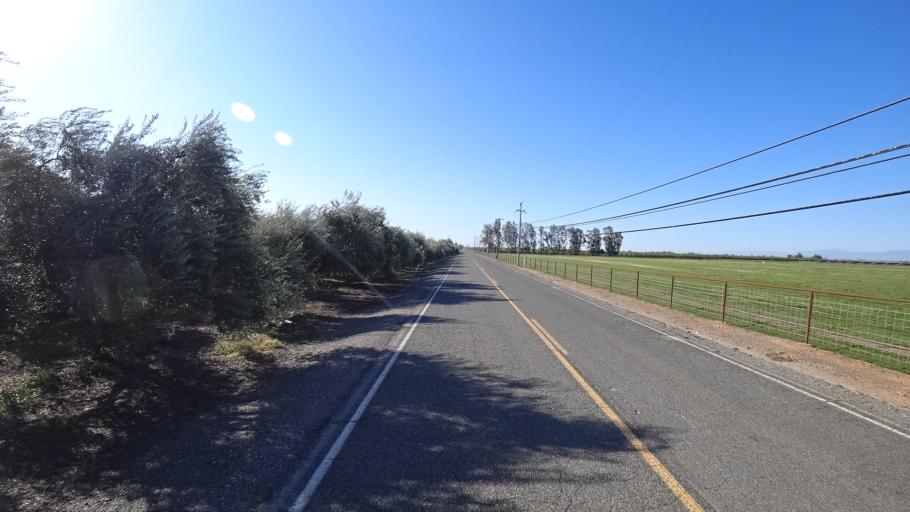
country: US
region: California
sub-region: Glenn County
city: Orland
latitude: 39.7888
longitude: -122.1041
